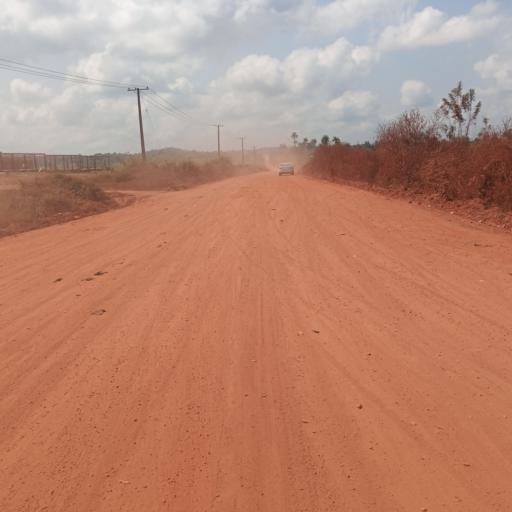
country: NG
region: Osun
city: Ile-Ife
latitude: 7.4043
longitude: 4.5662
